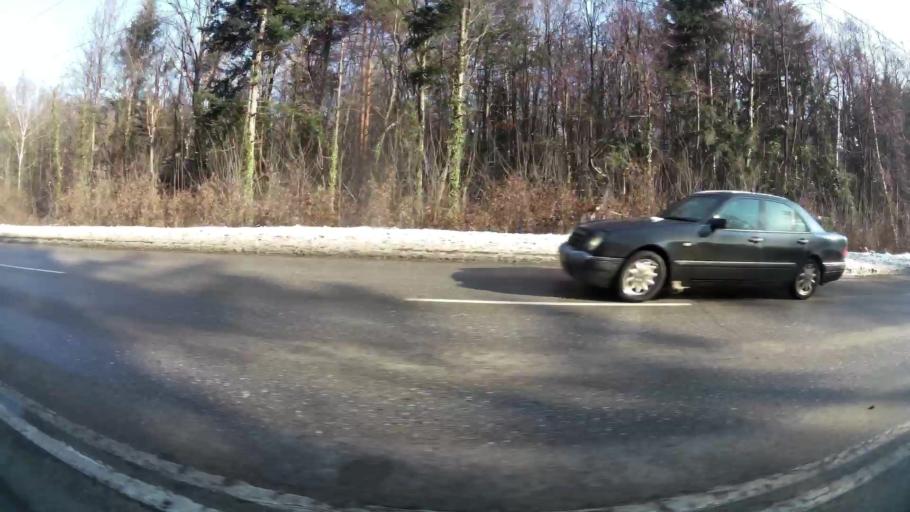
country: BG
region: Sofia-Capital
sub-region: Stolichna Obshtina
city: Sofia
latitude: 42.6642
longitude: 23.3372
